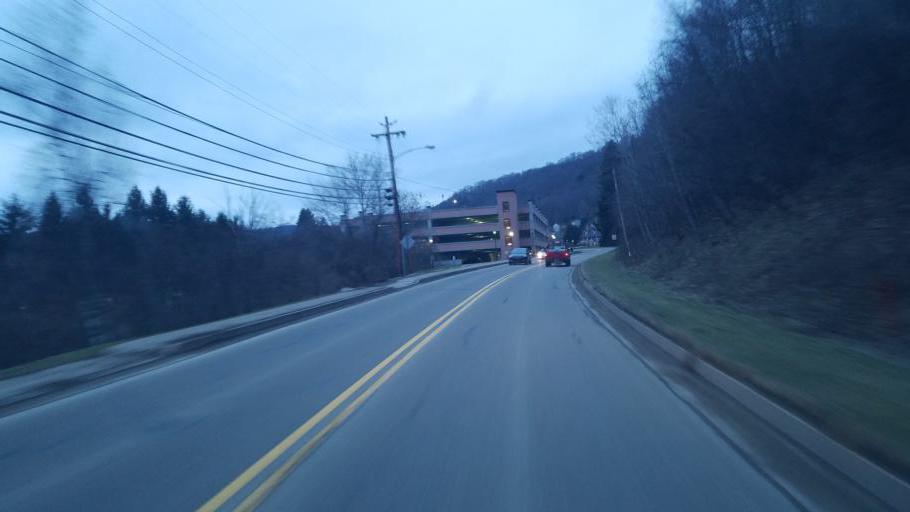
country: US
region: Pennsylvania
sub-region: Potter County
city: Coudersport
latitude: 41.7826
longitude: -78.0186
